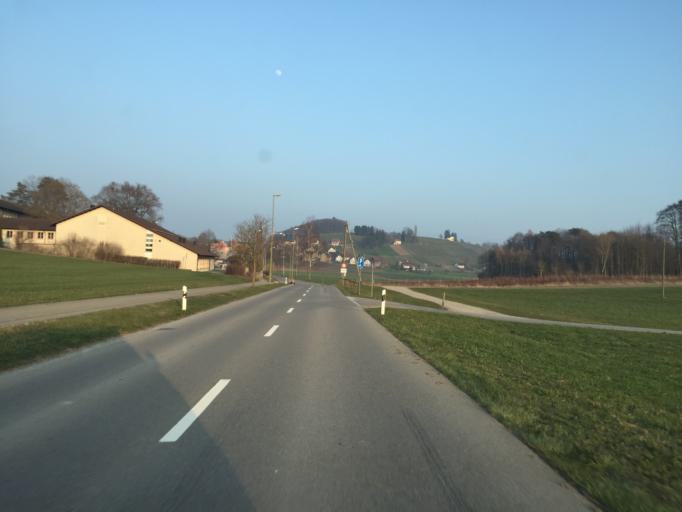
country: CH
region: Zurich
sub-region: Bezirk Andelfingen
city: Marthalen
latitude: 47.6379
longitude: 8.6807
